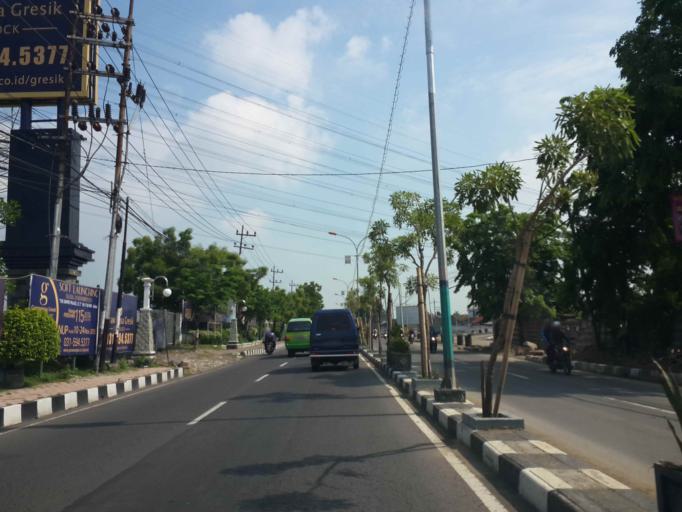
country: ID
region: East Java
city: Kebomas
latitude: -7.1856
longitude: 112.6479
